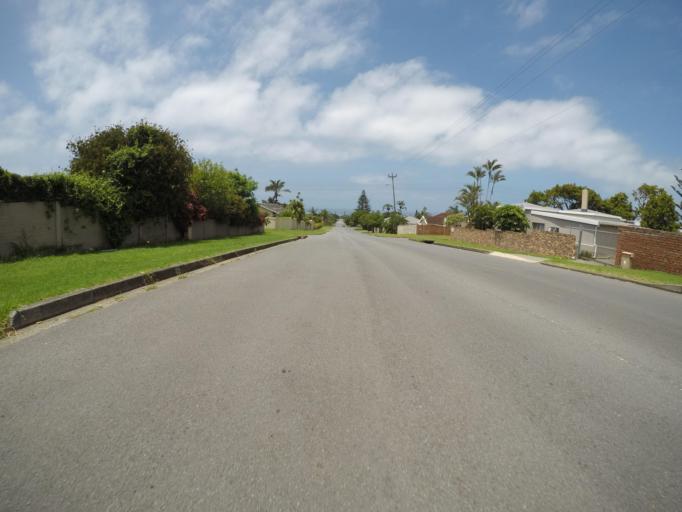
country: ZA
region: Eastern Cape
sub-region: Buffalo City Metropolitan Municipality
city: East London
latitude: -32.9408
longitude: 28.0093
